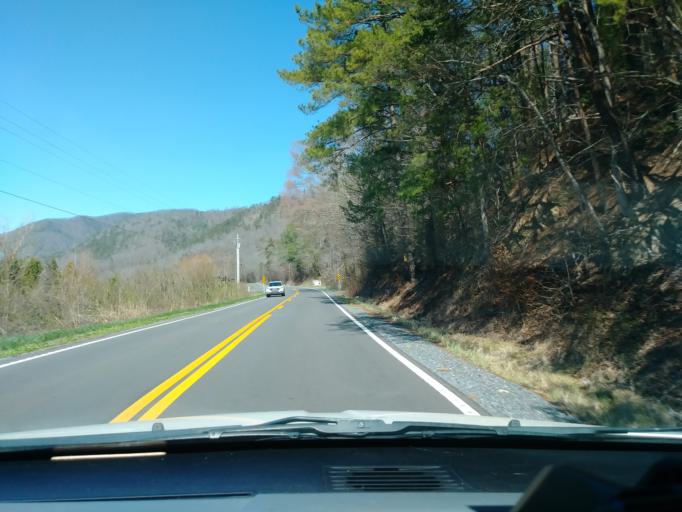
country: US
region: Tennessee
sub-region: Cocke County
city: Newport
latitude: 35.9172
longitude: -82.9891
